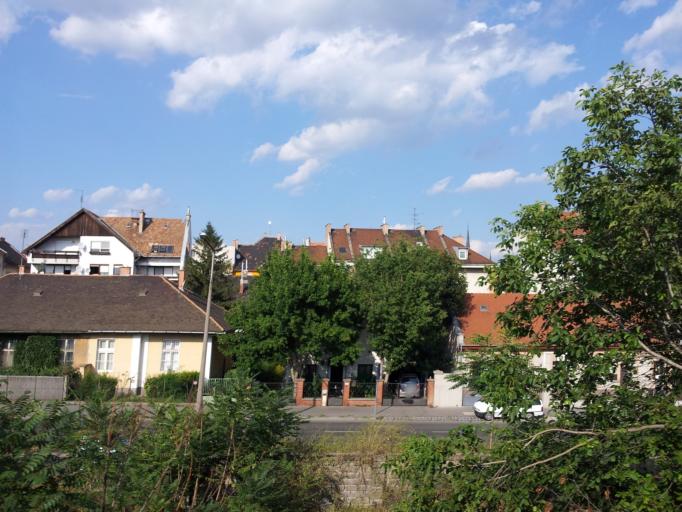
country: HU
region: Budapest
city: Budapest X. keruelet
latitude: 47.4787
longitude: 19.1305
